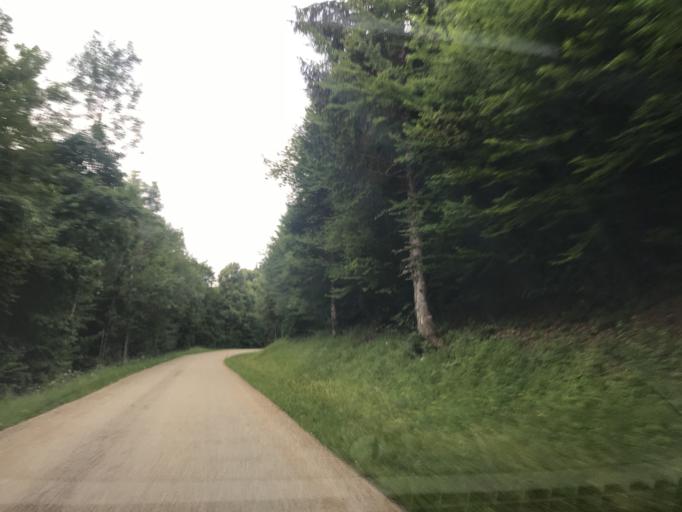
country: FR
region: Rhone-Alpes
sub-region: Departement de l'Isere
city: Le Touvet
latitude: 45.3699
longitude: 5.9222
